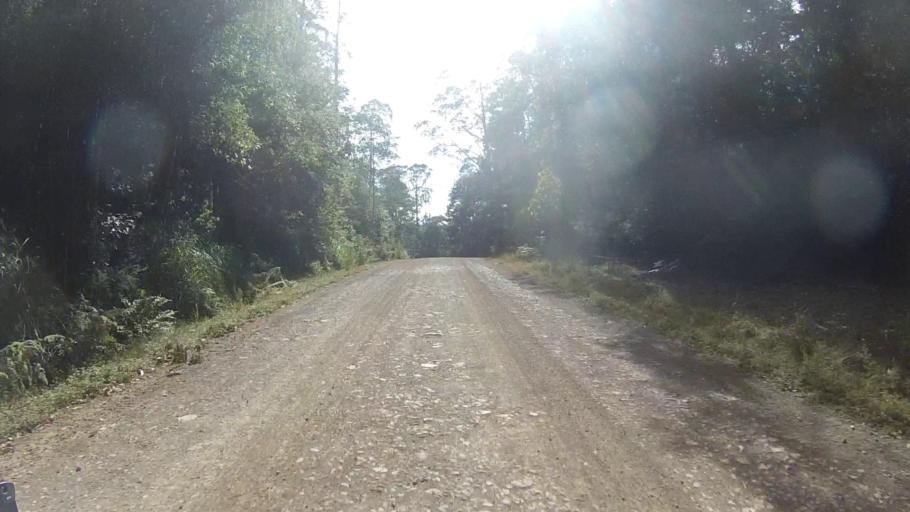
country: AU
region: Tasmania
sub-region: Sorell
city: Sorell
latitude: -42.7387
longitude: 147.8316
